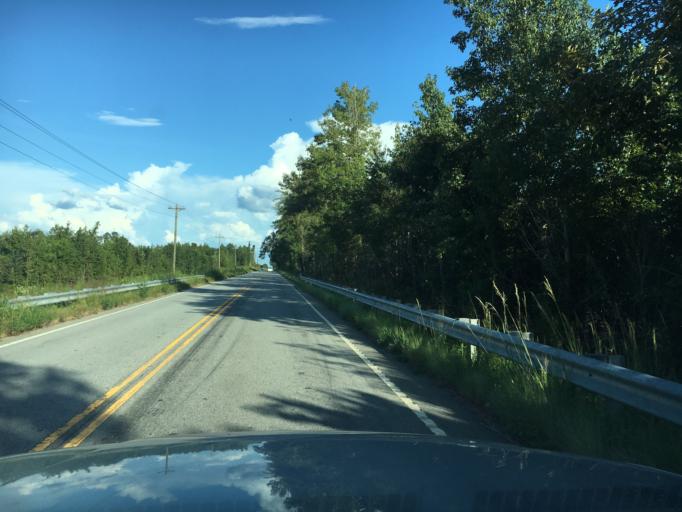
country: US
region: South Carolina
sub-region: Greenville County
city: Five Forks
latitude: 34.7996
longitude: -82.1525
